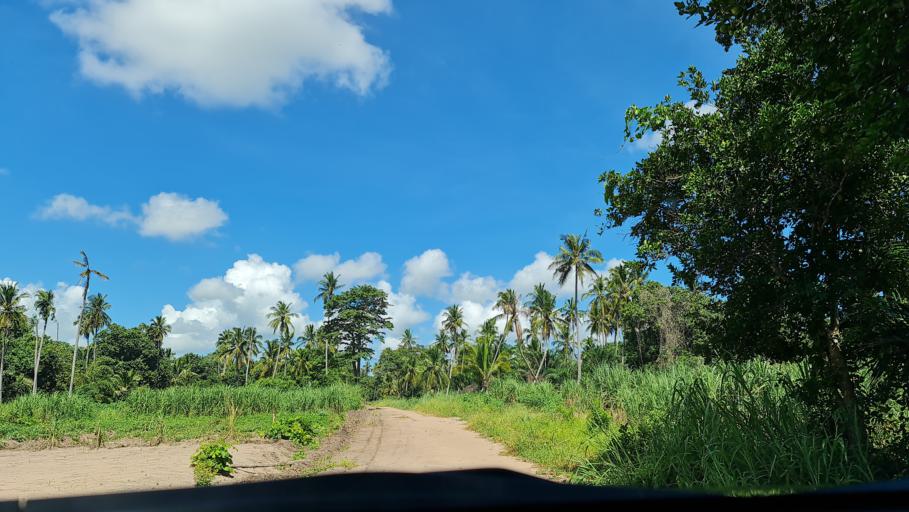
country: MZ
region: Zambezia
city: Quelimane
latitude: -17.3842
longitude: 37.5291
